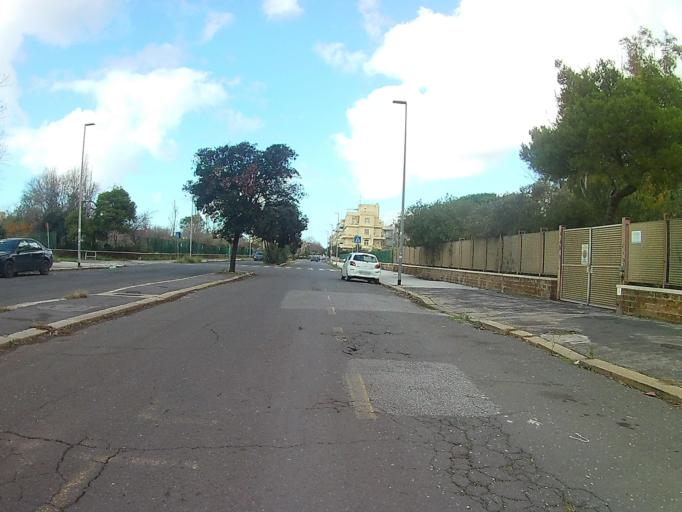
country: IT
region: Latium
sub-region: Citta metropolitana di Roma Capitale
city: Lido di Ostia
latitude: 41.7279
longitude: 12.2894
